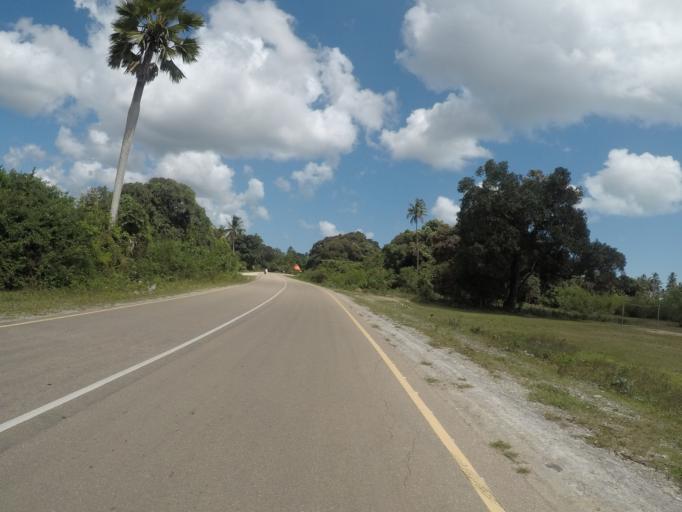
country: TZ
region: Zanzibar Central/South
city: Koani
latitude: -6.2327
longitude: 39.3594
